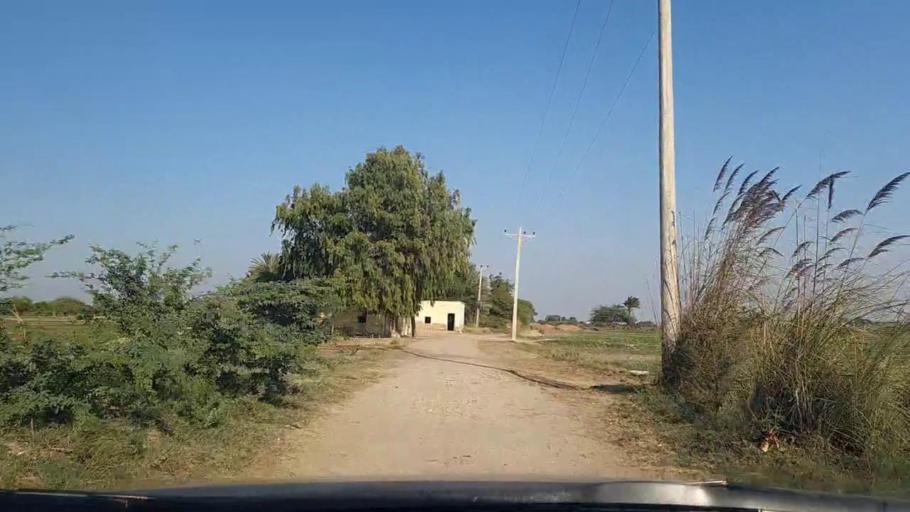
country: PK
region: Sindh
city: Mirpur Sakro
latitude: 24.5411
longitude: 67.6430
